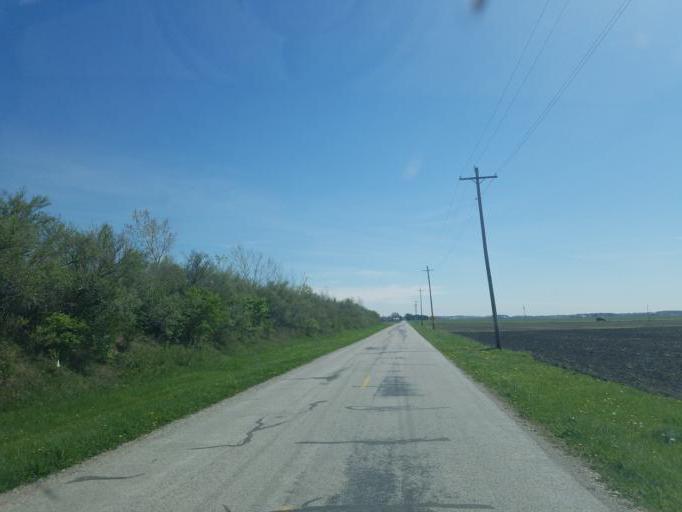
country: US
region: Ohio
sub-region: Huron County
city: Bellevue
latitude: 41.3283
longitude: -82.7931
